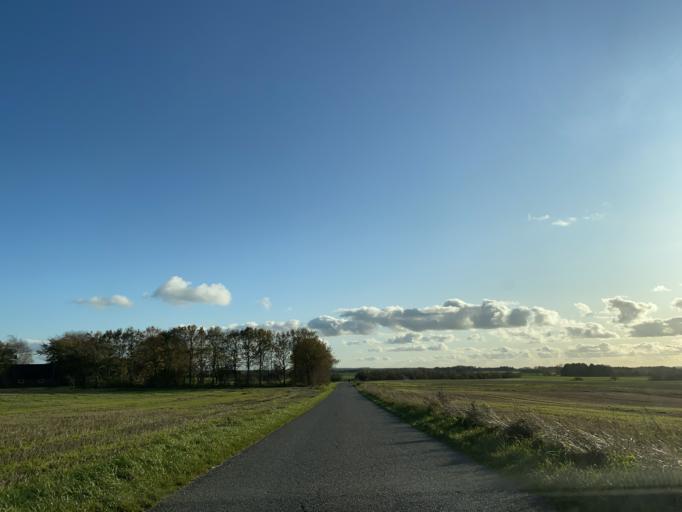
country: DK
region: Central Jutland
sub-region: Viborg Kommune
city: Bjerringbro
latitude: 56.3315
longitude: 9.7091
